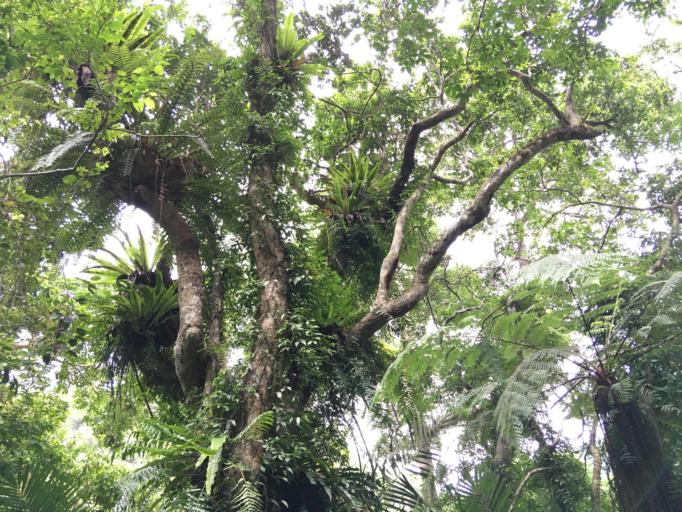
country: TW
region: Taiwan
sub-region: Yilan
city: Yilan
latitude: 24.4245
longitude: 121.6952
